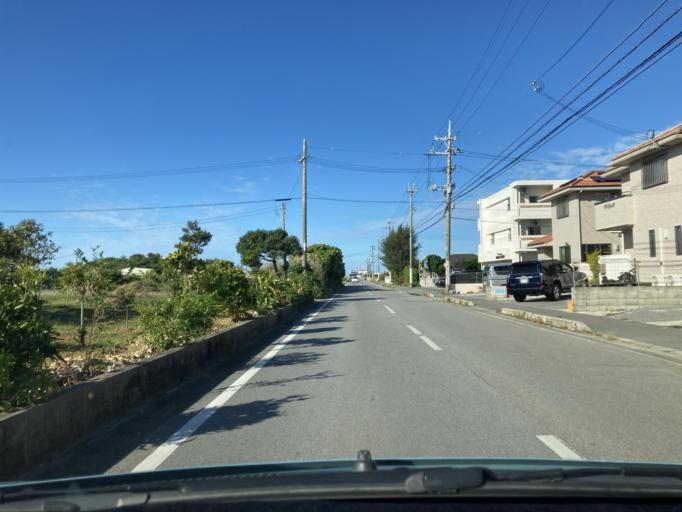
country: JP
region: Okinawa
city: Chatan
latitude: 26.3707
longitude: 127.7444
